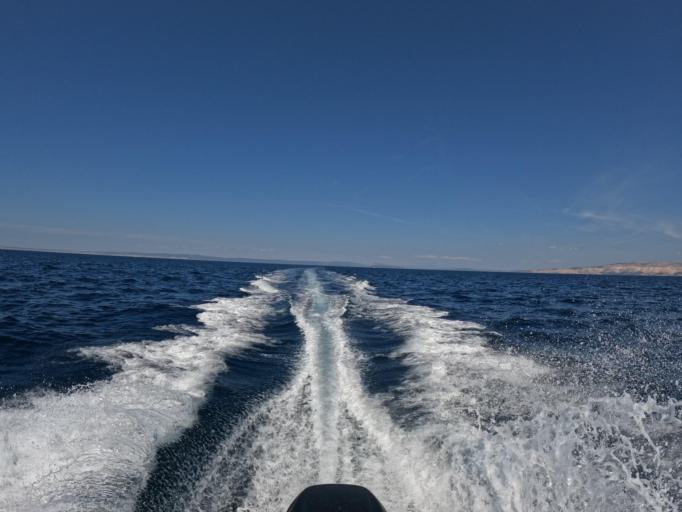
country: HR
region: Primorsko-Goranska
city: Lopar
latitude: 44.8600
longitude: 14.6927
